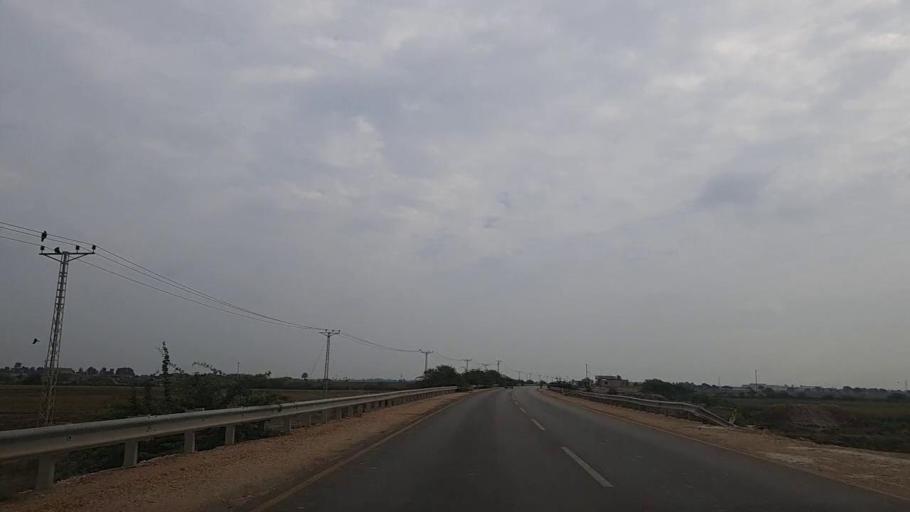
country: PK
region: Sindh
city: Thatta
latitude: 24.6184
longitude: 68.0751
